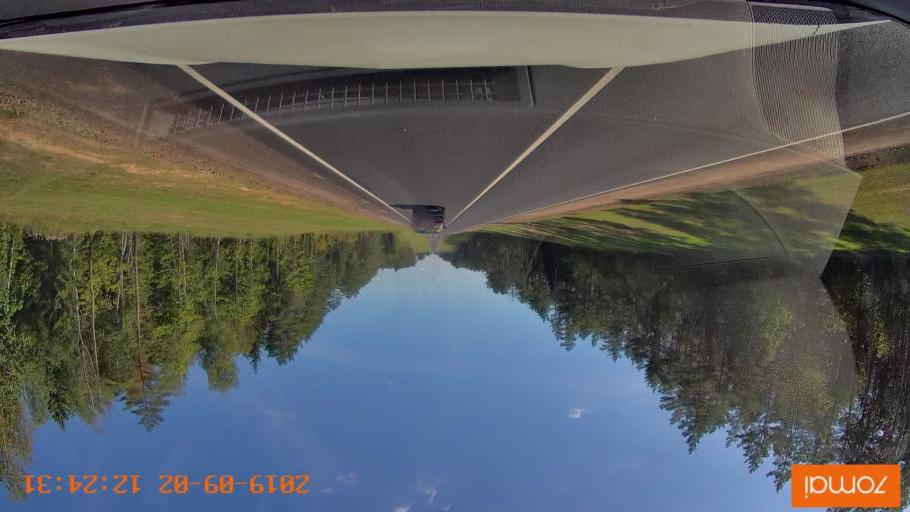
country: RU
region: Smolensk
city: Shumyachi
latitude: 53.8677
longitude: 32.6065
